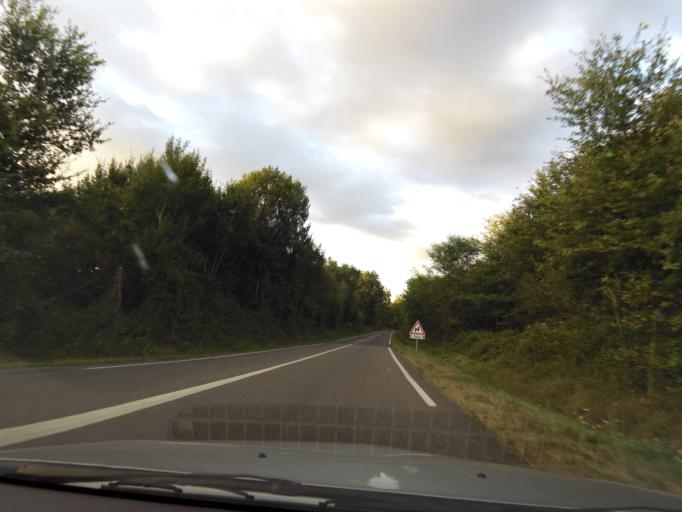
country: FR
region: Aquitaine
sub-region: Departement de la Gironde
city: Castets-en-Dorthe
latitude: 44.5156
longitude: -0.1829
